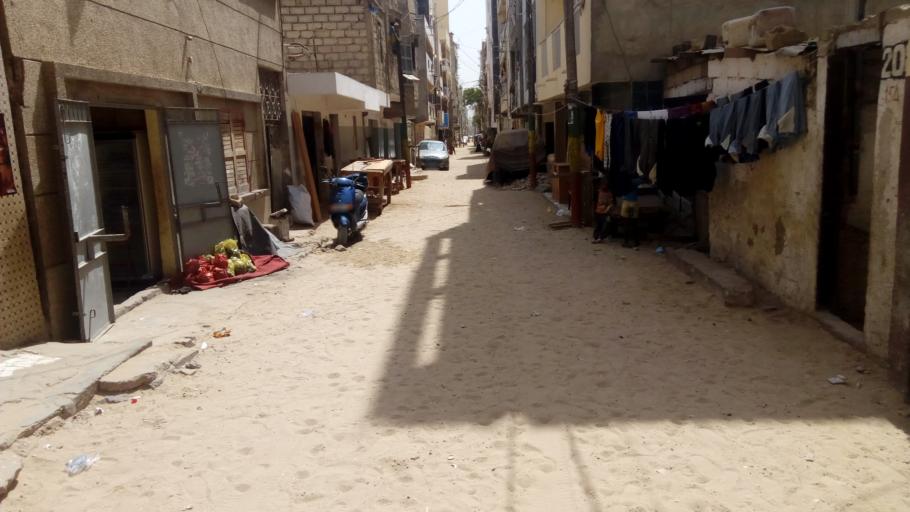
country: SN
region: Dakar
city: Grand Dakar
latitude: 14.7144
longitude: -17.4488
